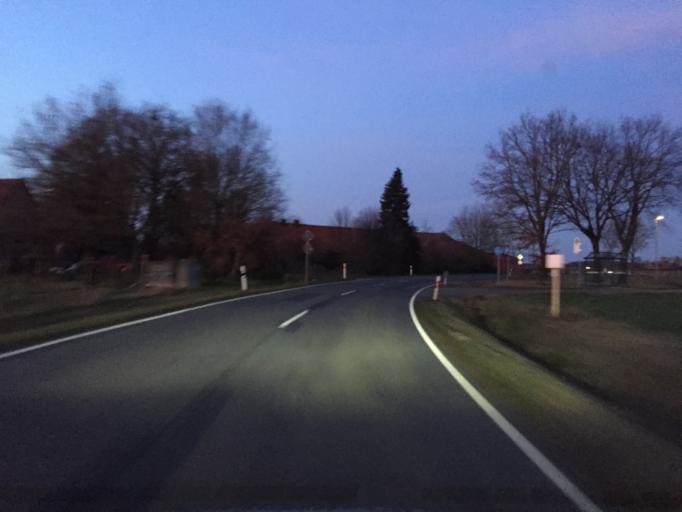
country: DE
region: Lower Saxony
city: Kirchdorf
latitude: 52.6196
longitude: 8.8799
